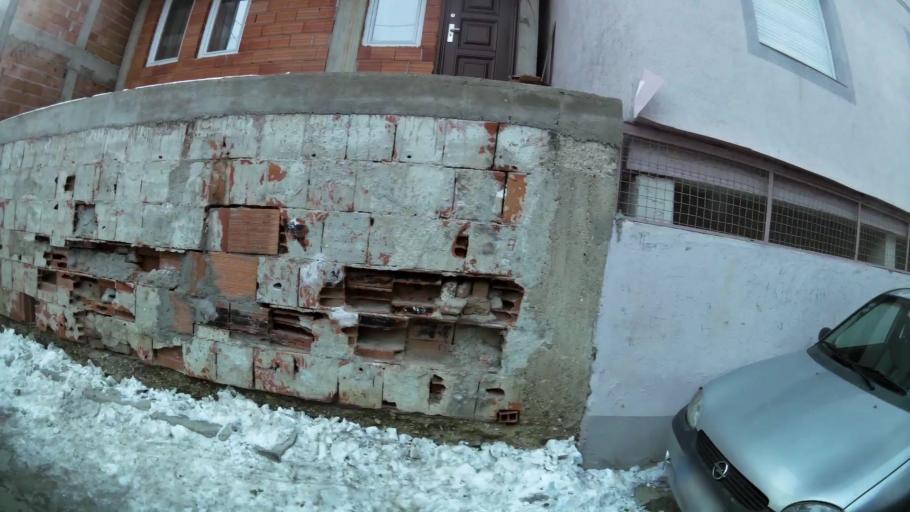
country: MK
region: Cair
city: Cair
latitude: 42.0042
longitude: 21.4483
